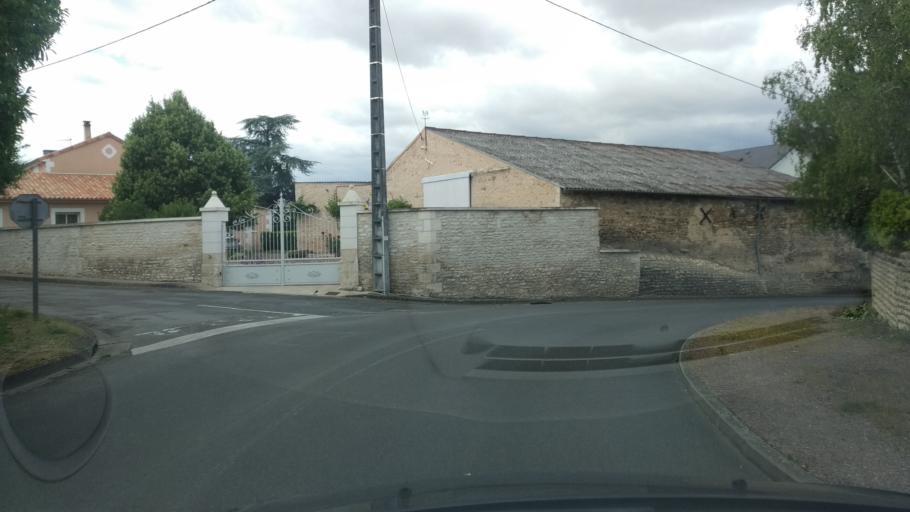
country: FR
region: Poitou-Charentes
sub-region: Departement de la Vienne
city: Vouille
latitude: 46.6311
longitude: 0.1829
